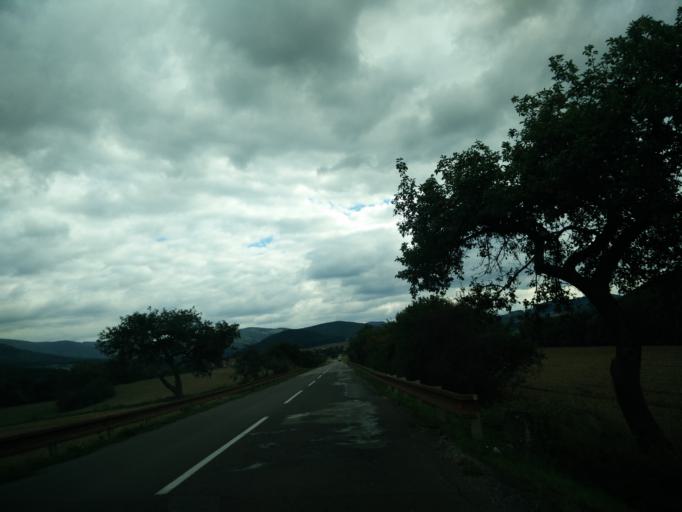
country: SK
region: Nitriansky
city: Partizanske
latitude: 48.6151
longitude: 18.4785
